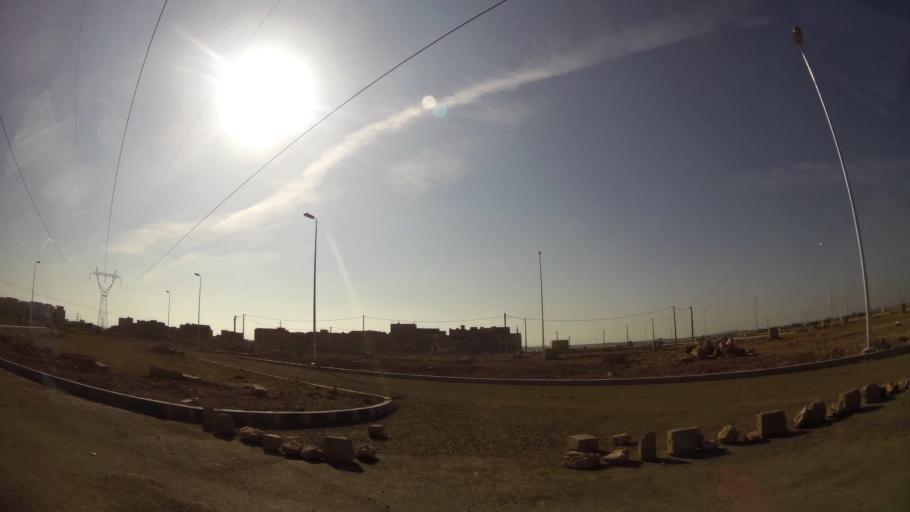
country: MA
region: Oriental
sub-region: Oujda-Angad
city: Oujda
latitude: 34.7238
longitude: -1.8854
